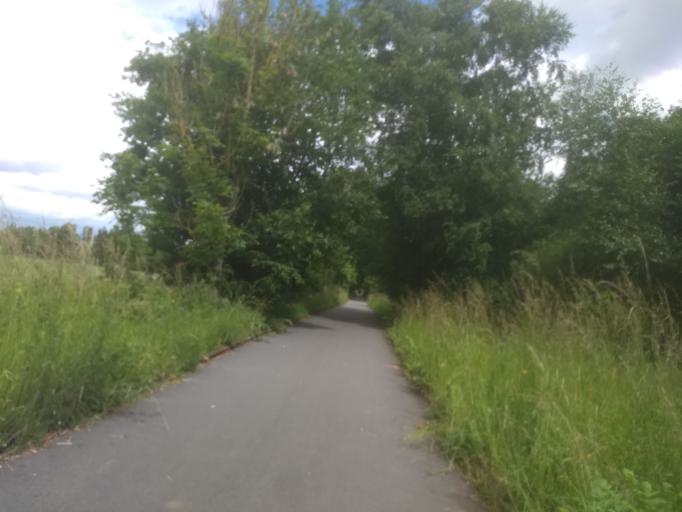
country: FR
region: Nord-Pas-de-Calais
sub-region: Departement du Pas-de-Calais
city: Beaumetz-les-Loges
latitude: 50.2380
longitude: 2.6583
